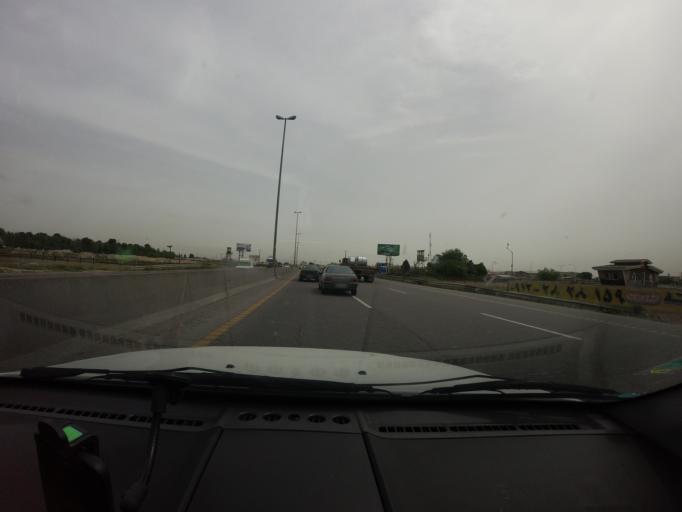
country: IR
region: Tehran
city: Robat Karim
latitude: 35.5426
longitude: 51.1152
